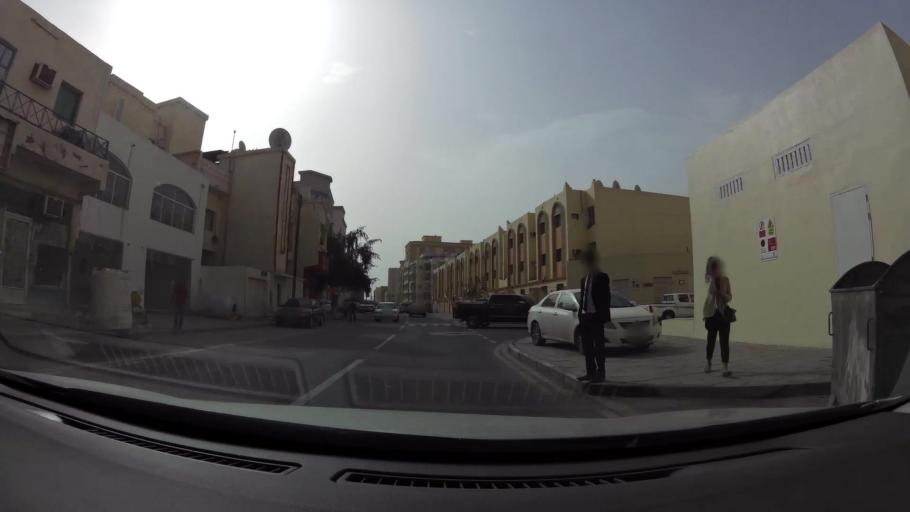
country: QA
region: Baladiyat ad Dawhah
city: Doha
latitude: 25.2776
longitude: 51.5435
